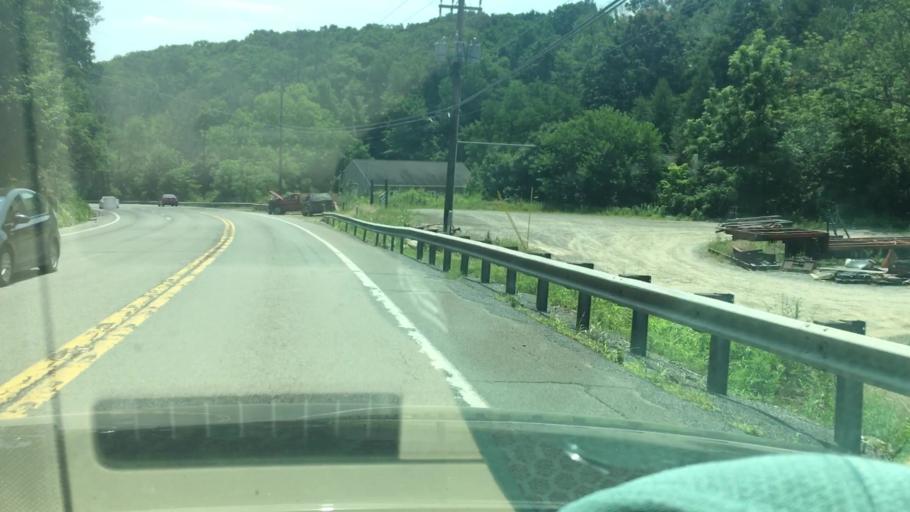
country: US
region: Pennsylvania
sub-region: Schuylkill County
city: Coaldale
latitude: 40.7481
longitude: -75.9015
